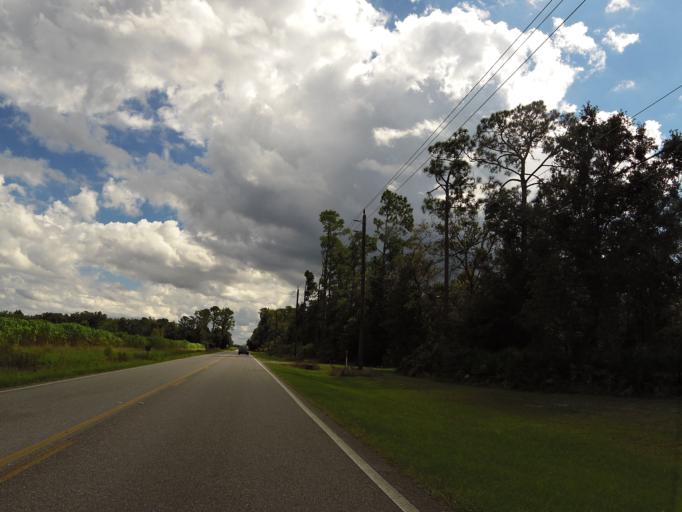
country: US
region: Florida
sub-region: Saint Johns County
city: Saint Augustine South
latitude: 29.8155
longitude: -81.4847
